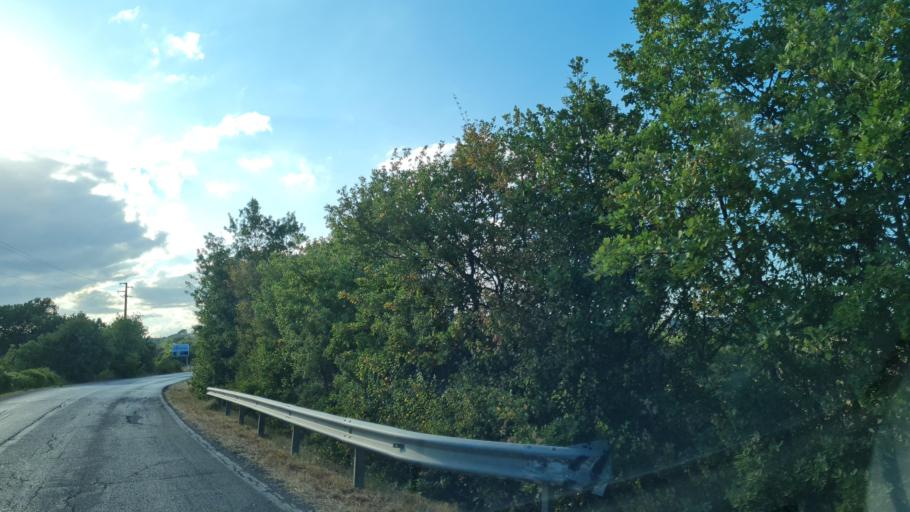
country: IT
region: Tuscany
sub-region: Provincia di Siena
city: Sarteano
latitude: 43.0311
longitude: 11.8544
